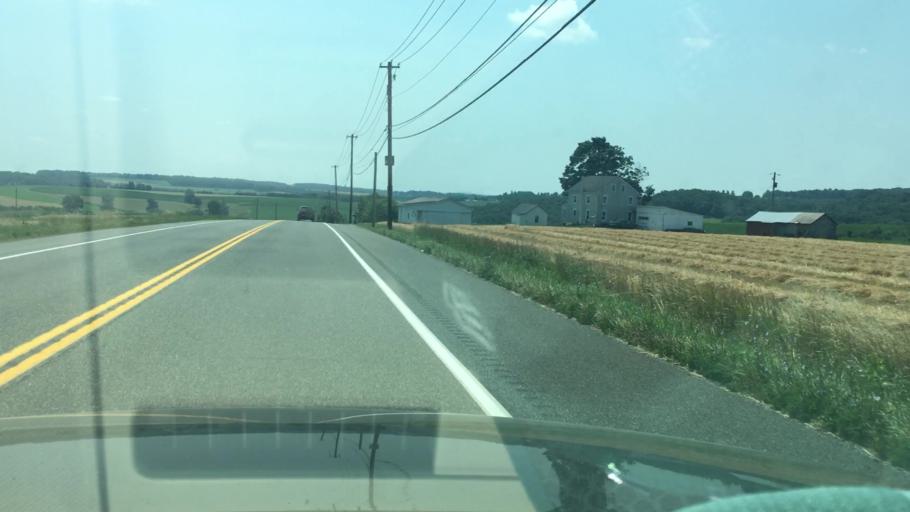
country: US
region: Pennsylvania
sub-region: Lehigh County
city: Schnecksville
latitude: 40.6440
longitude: -75.6827
